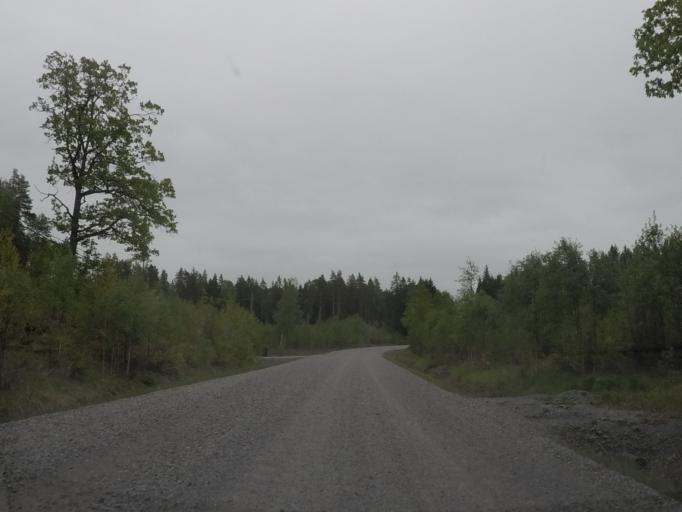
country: SE
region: Soedermanland
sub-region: Flens Kommun
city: Halleforsnas
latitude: 59.1899
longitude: 16.4889
